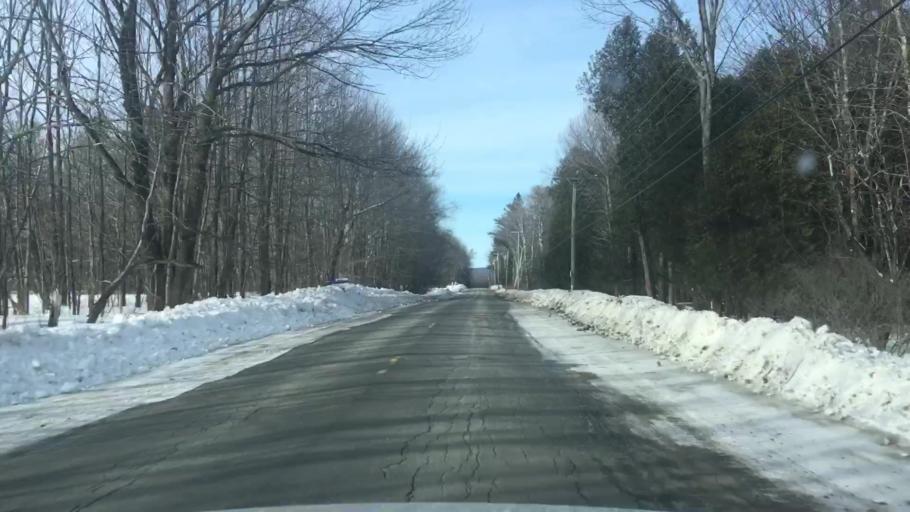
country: US
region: Maine
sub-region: Penobscot County
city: Charleston
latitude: 45.0336
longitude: -69.0320
